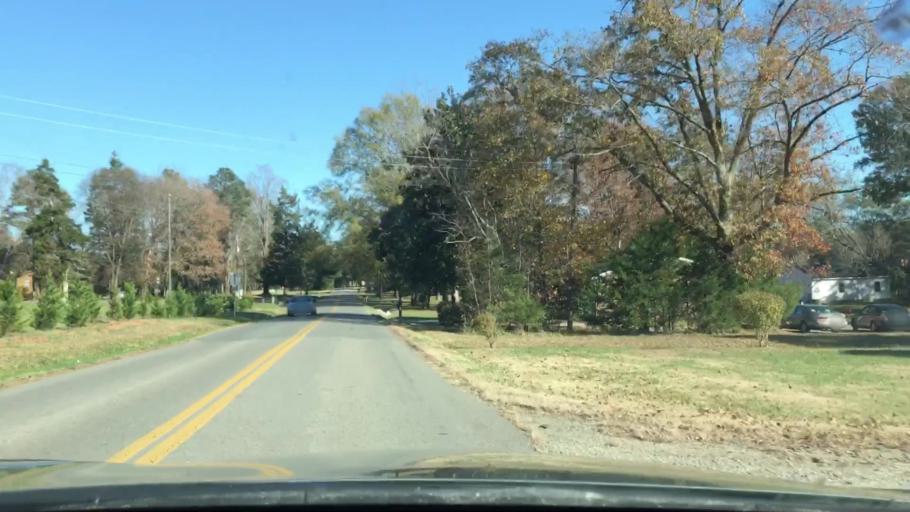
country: US
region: Virginia
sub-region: Henrico County
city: Short Pump
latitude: 37.6664
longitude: -77.7098
